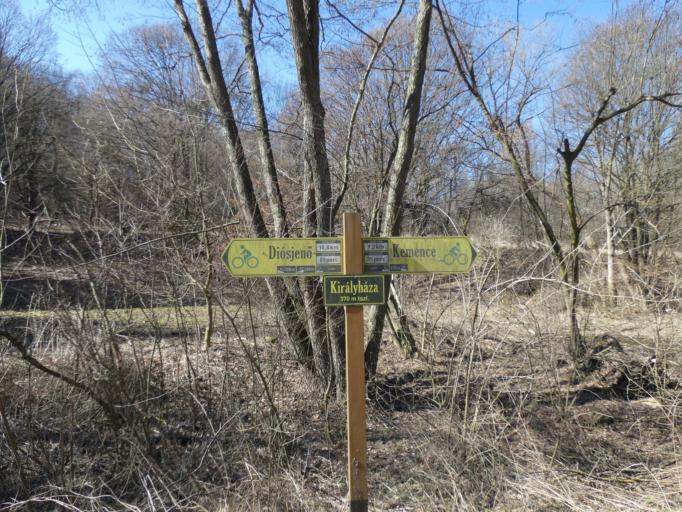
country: SK
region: Nitriansky
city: Sahy
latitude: 47.9881
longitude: 18.9690
